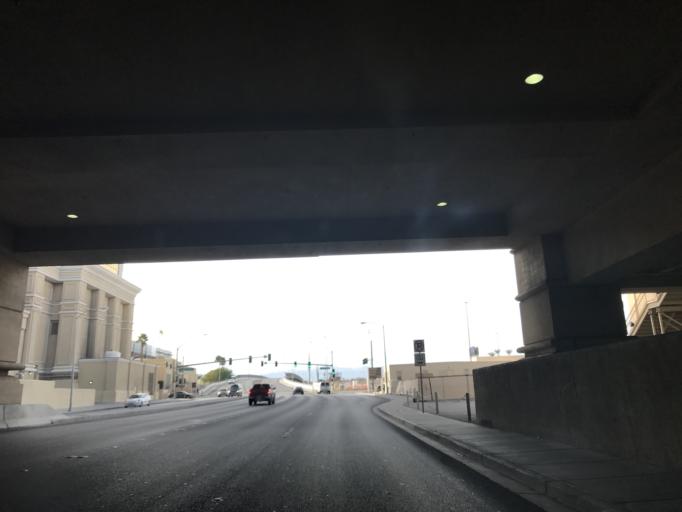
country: US
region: Nevada
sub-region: Clark County
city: Paradise
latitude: 36.0938
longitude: -115.1766
